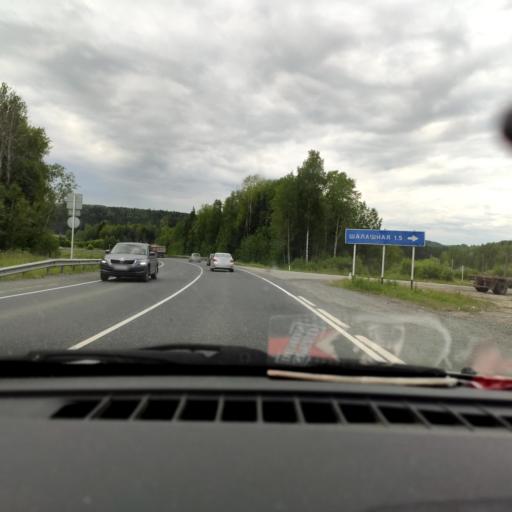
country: RU
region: Perm
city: Verkhnechusovskiye Gorodki
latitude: 58.2905
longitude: 56.8967
